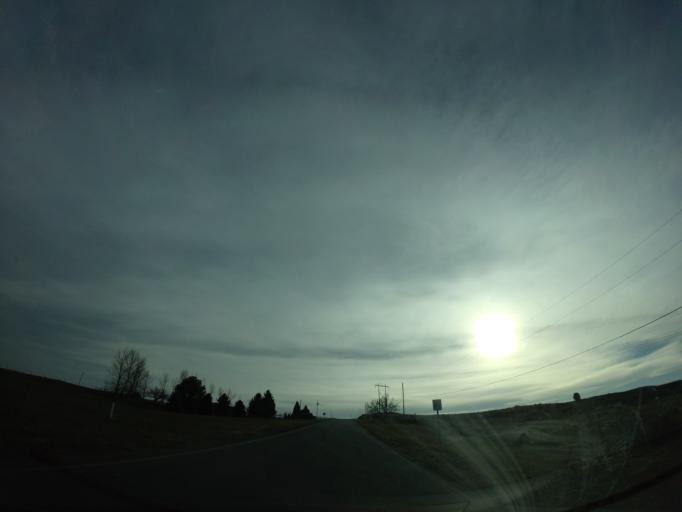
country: US
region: Montana
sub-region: Yellowstone County
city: Billings
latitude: 45.7944
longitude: -108.4556
